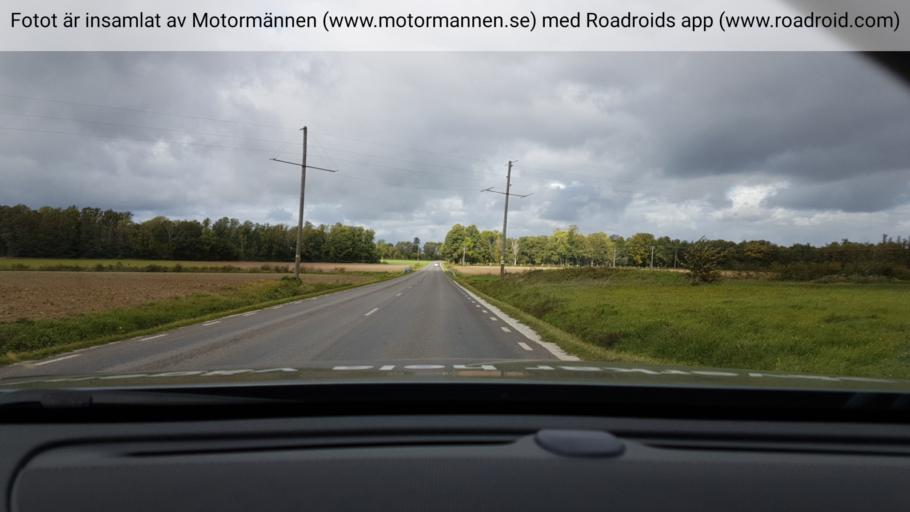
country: SE
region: Gotland
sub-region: Gotland
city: Vibble
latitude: 57.4720
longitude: 18.3602
